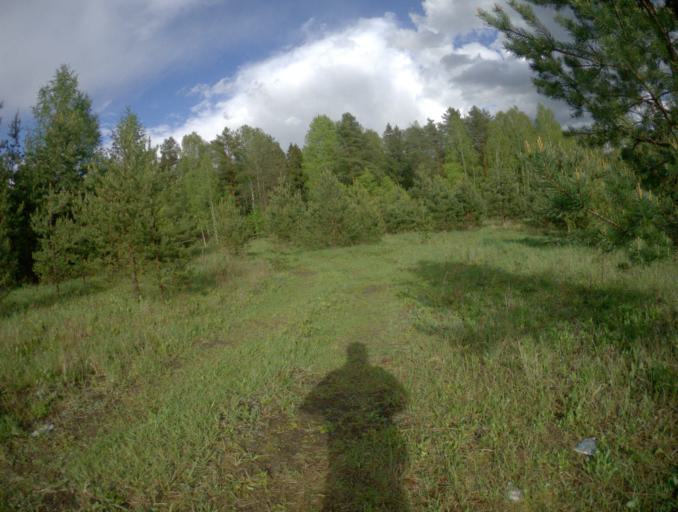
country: RU
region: Vladimir
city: Gusevskiy
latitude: 55.5767
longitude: 40.5136
